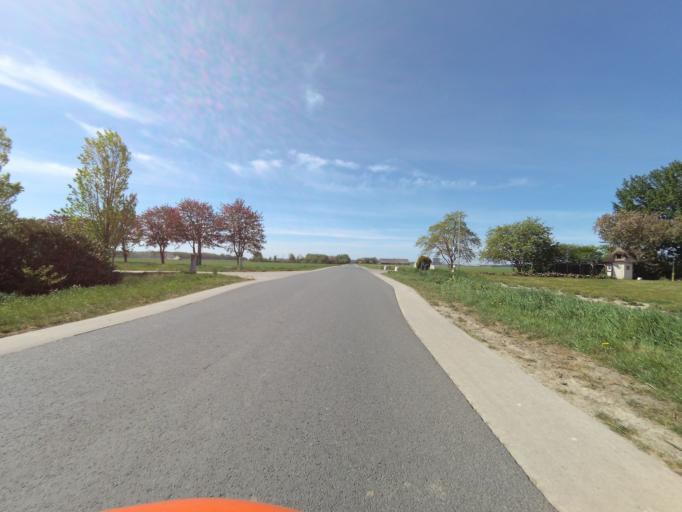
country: NL
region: Flevoland
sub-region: Gemeente Dronten
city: Biddinghuizen
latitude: 52.4204
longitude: 5.6699
